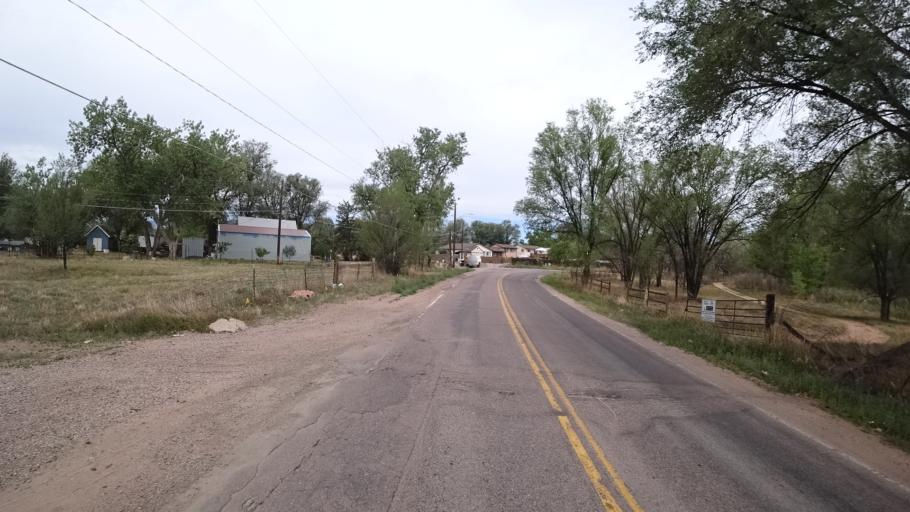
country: US
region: Colorado
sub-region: El Paso County
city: Fountain
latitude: 38.6764
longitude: -104.7006
